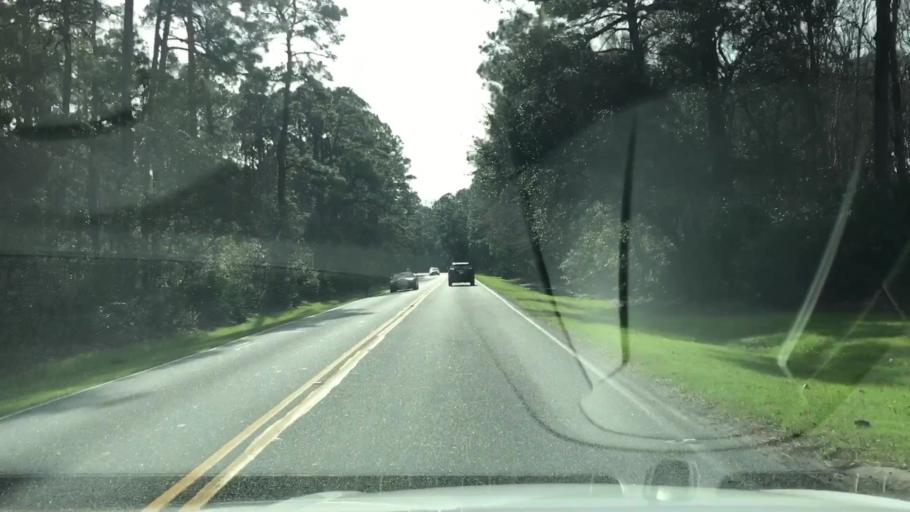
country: US
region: South Carolina
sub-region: Beaufort County
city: Hilton Head Island
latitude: 32.2372
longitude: -80.7225
